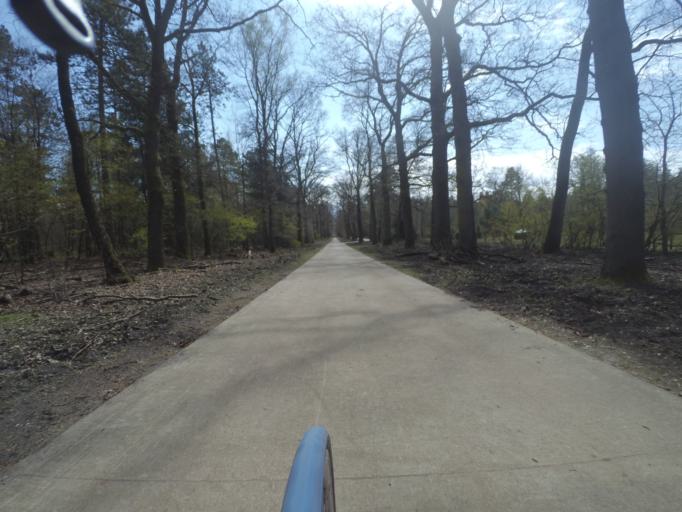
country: NL
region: Gelderland
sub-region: Gemeente Nunspeet
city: Nunspeet
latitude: 52.3432
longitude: 5.8669
